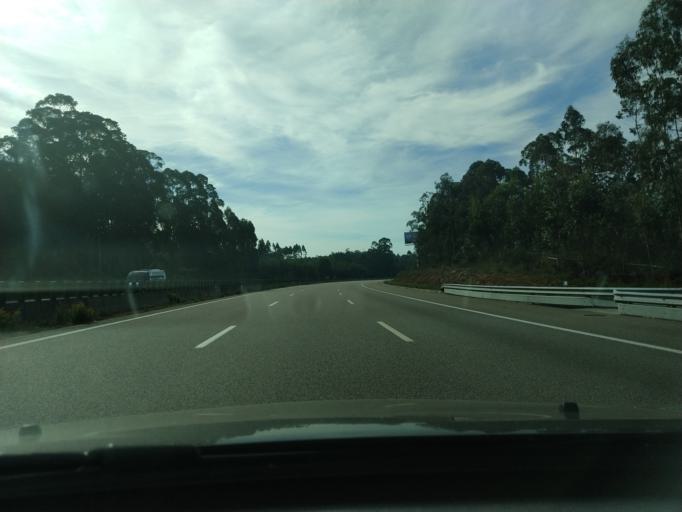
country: PT
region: Aveiro
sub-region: Ovar
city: Valega
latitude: 40.8573
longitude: -8.5556
